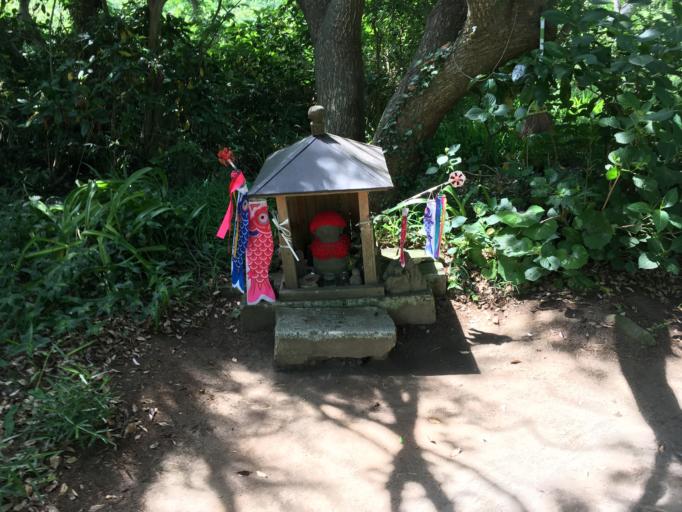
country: JP
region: Kanagawa
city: Kamakura
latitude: 35.3134
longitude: 139.5685
